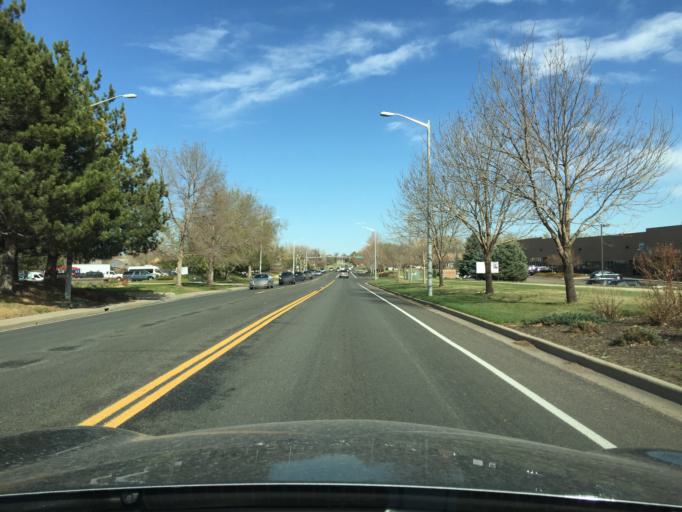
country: US
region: Colorado
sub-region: Boulder County
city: Longmont
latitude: 40.1379
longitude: -105.1245
